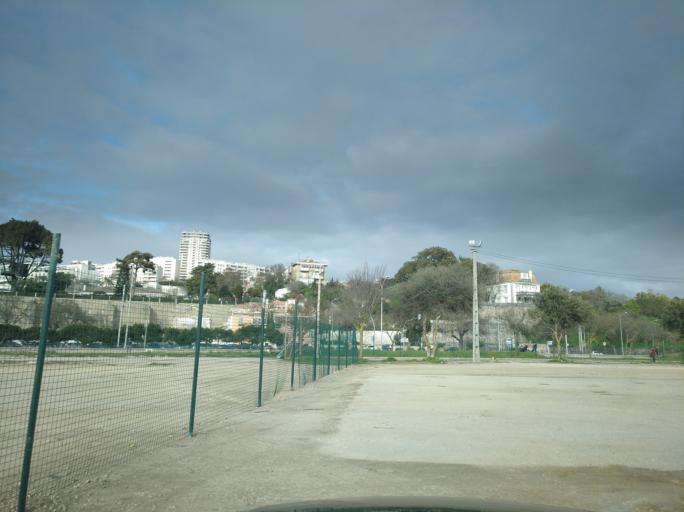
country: PT
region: Lisbon
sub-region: Oeiras
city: Alges
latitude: 38.6981
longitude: -9.2370
